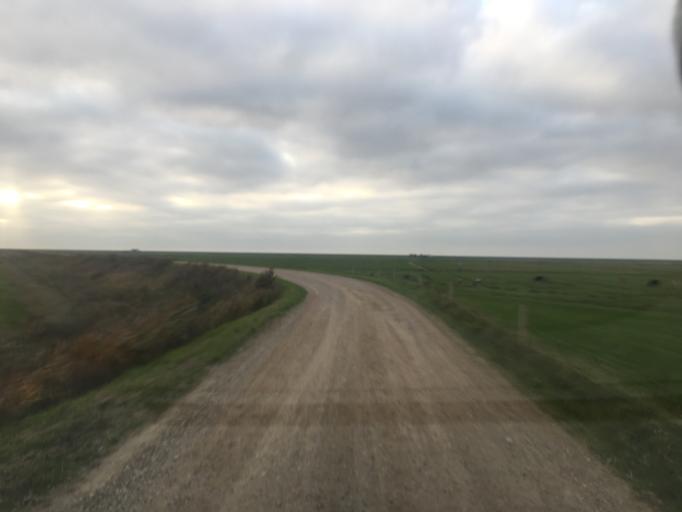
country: DE
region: Schleswig-Holstein
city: Rodenas
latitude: 54.9280
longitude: 8.6987
